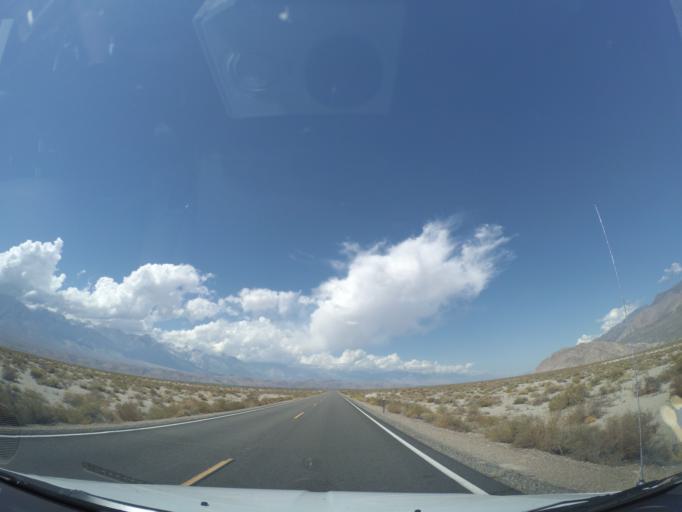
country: US
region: California
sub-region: Inyo County
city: Lone Pine
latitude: 36.5668
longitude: -117.9811
